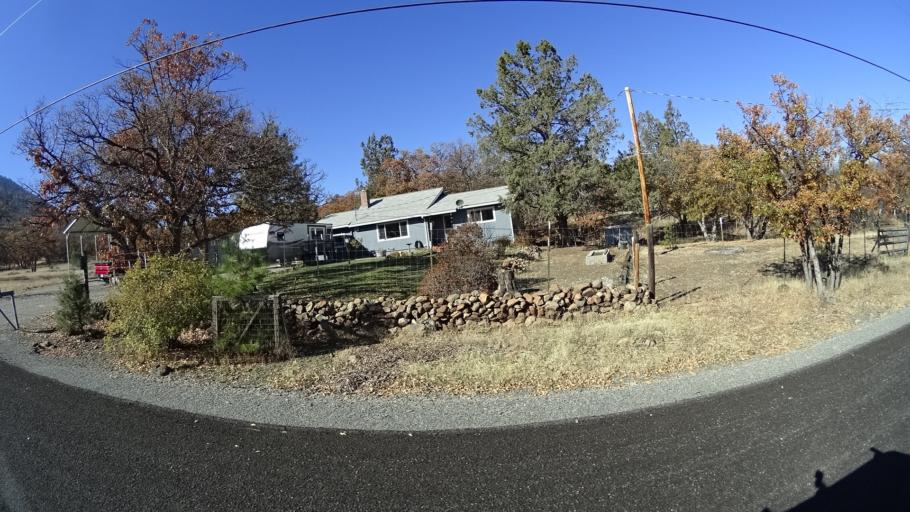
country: US
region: California
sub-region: Siskiyou County
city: Montague
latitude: 41.8794
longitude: -122.4867
